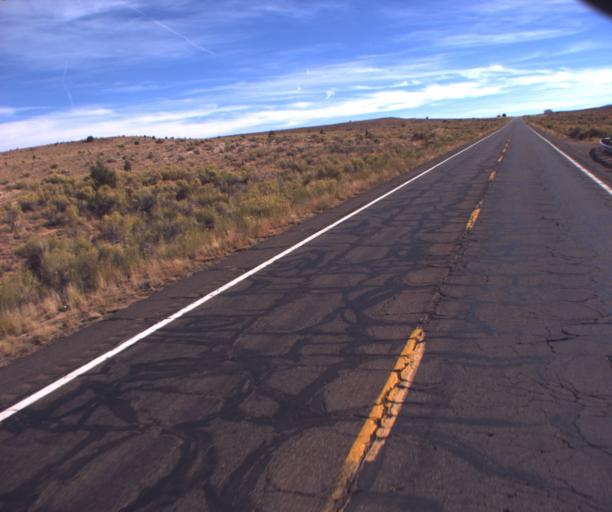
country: US
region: Arizona
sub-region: Coconino County
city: Kaibito
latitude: 36.6133
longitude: -111.0656
